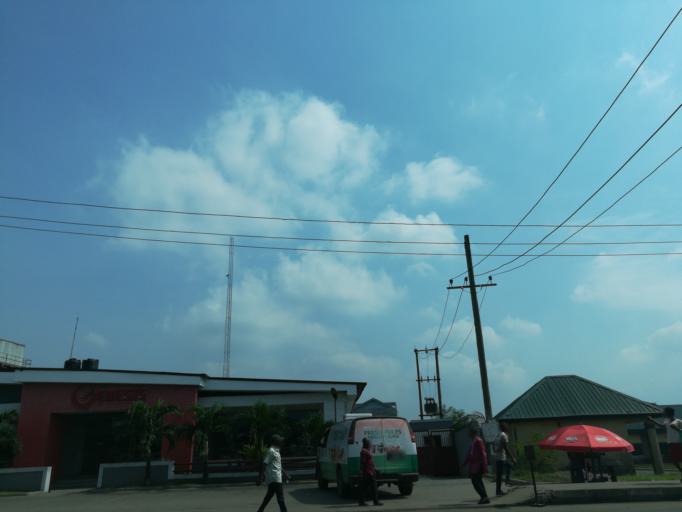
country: NG
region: Rivers
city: Port Harcourt
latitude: 4.8068
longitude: 6.9875
